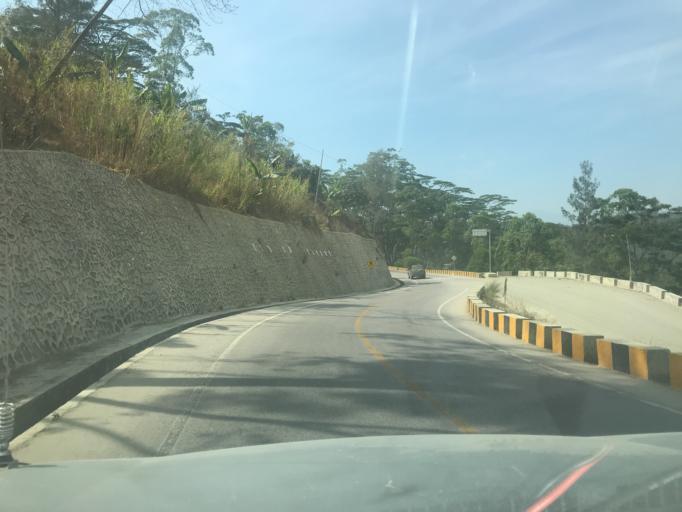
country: TL
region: Aileu
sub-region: Aileu Villa
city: Aileu
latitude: -8.6760
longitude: 125.5507
